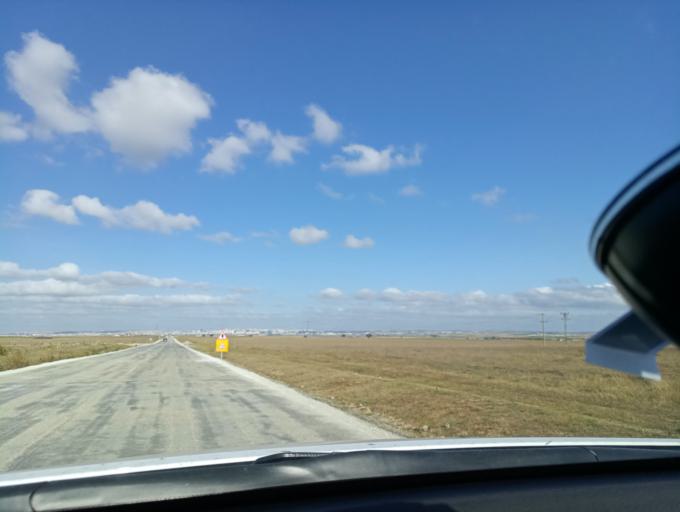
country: TR
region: Tekirdag
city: Corlu
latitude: 41.0656
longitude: 27.8339
